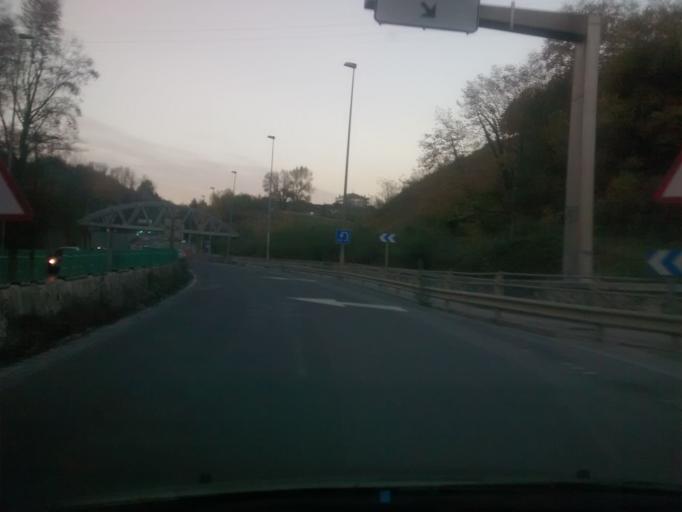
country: ES
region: Basque Country
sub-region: Provincia de Guipuzcoa
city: Hernani
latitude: 43.2870
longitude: -1.9979
